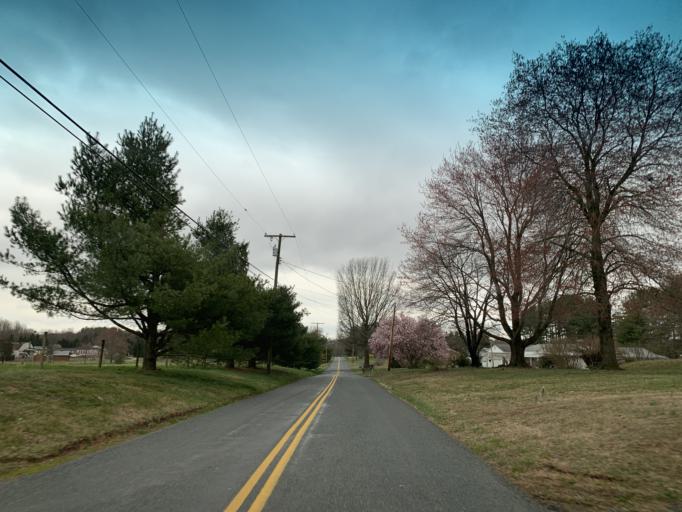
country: US
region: Maryland
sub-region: Harford County
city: Aberdeen
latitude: 39.5749
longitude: -76.1976
